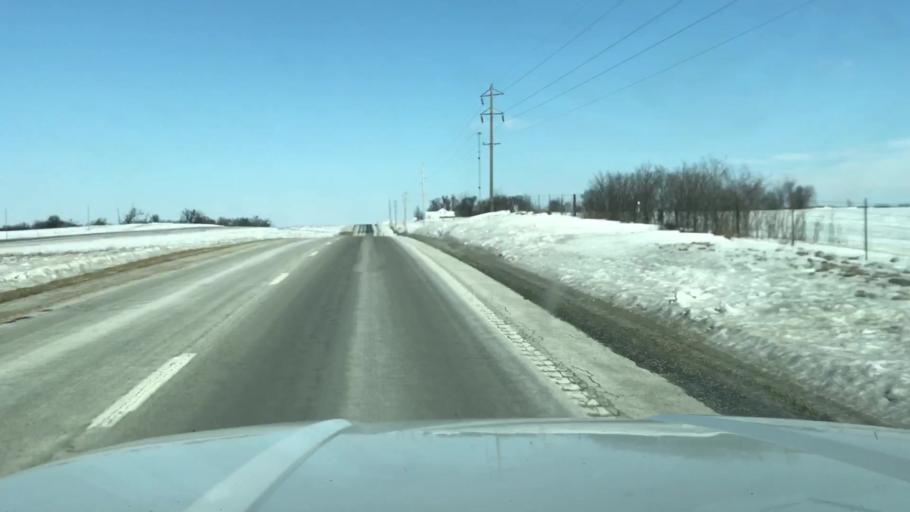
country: US
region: Missouri
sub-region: Nodaway County
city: Maryville
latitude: 40.1744
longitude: -94.8686
